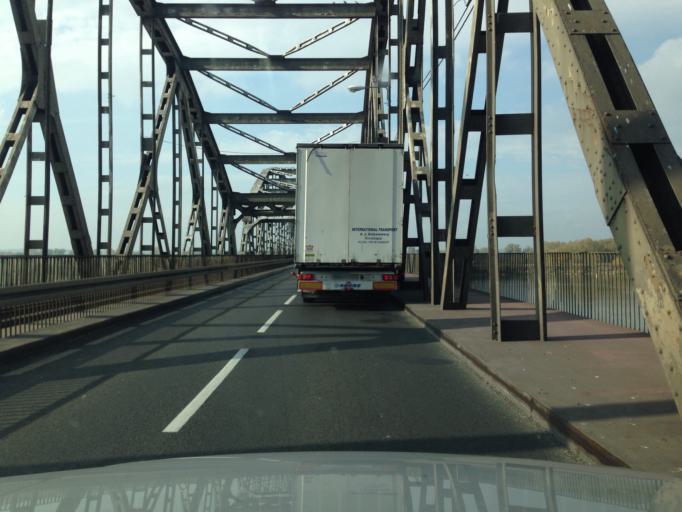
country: PL
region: Kujawsko-Pomorskie
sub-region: Grudziadz
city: Grudziadz
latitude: 53.4833
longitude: 18.7425
